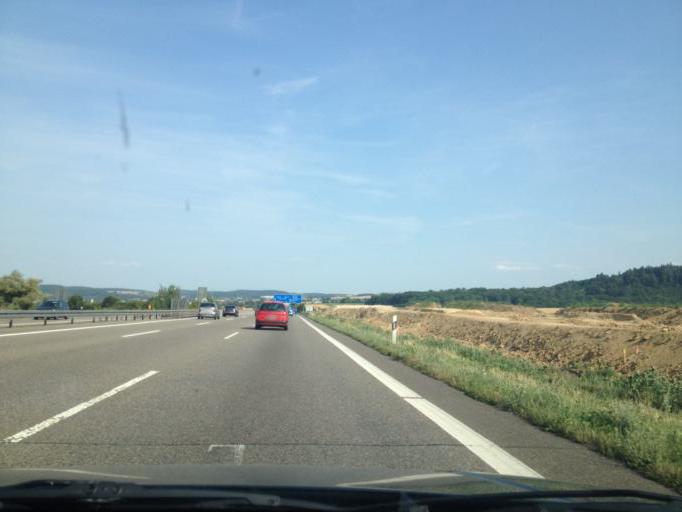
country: DE
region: Baden-Wuerttemberg
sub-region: Karlsruhe Region
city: Sinsheim
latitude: 49.2546
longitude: 8.8408
